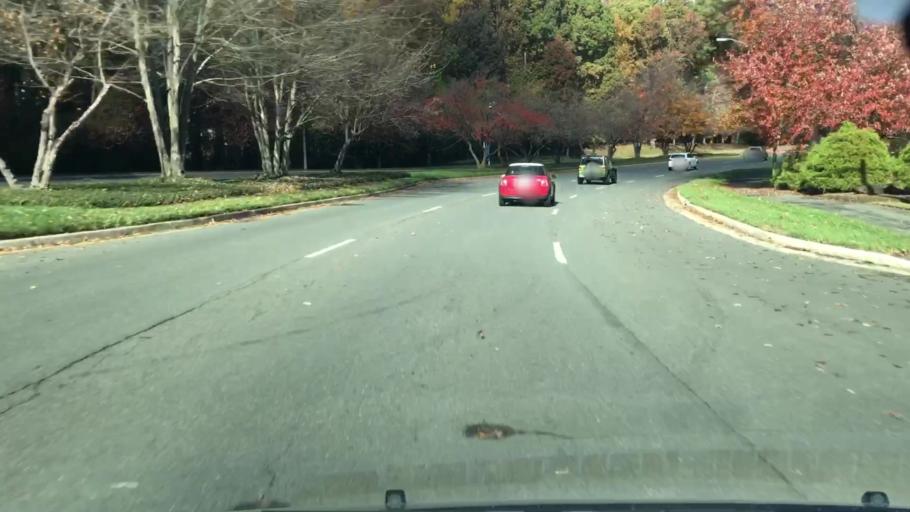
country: US
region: Virginia
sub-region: Fairfax County
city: Merrifield
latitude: 38.8694
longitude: -77.2171
